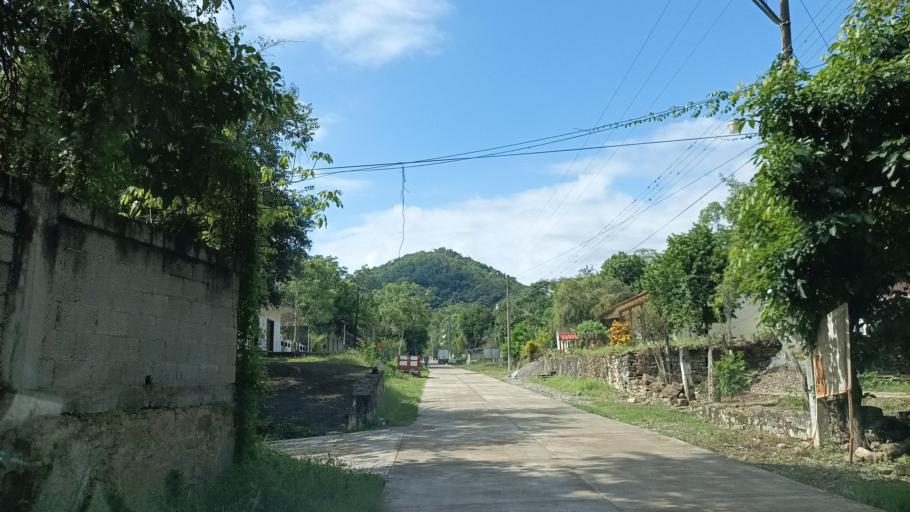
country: MX
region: Hidalgo
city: Huautla
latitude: 21.1339
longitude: -98.2500
